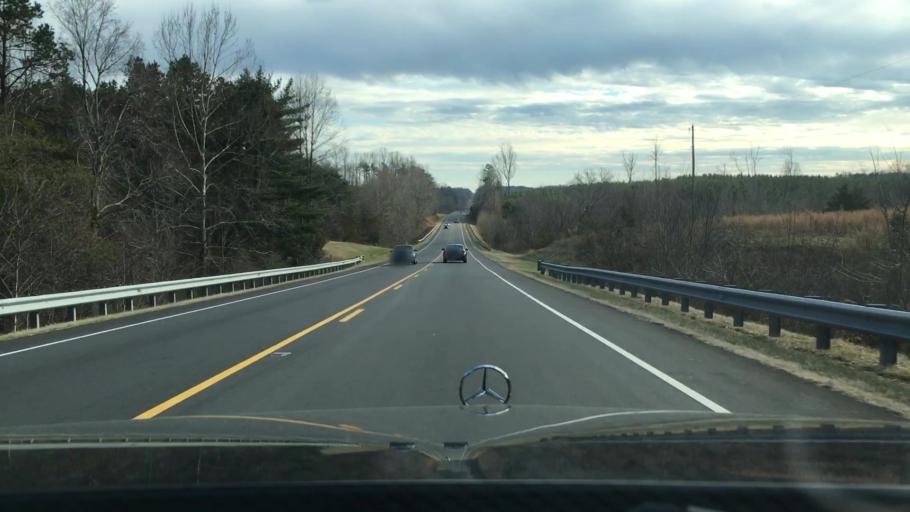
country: US
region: Virginia
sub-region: City of Danville
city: Danville
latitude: 36.5196
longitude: -79.3945
